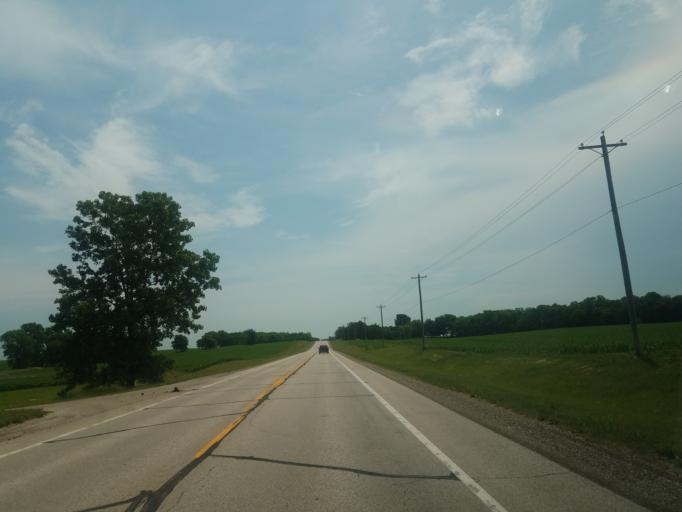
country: US
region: Illinois
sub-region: McLean County
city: Bloomington
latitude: 40.4432
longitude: -88.9464
